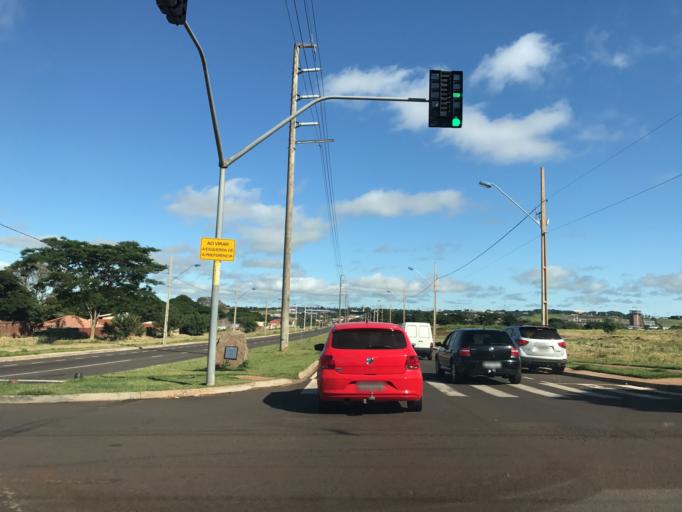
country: BR
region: Parana
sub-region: Maringa
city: Maringa
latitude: -23.4502
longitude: -51.9614
